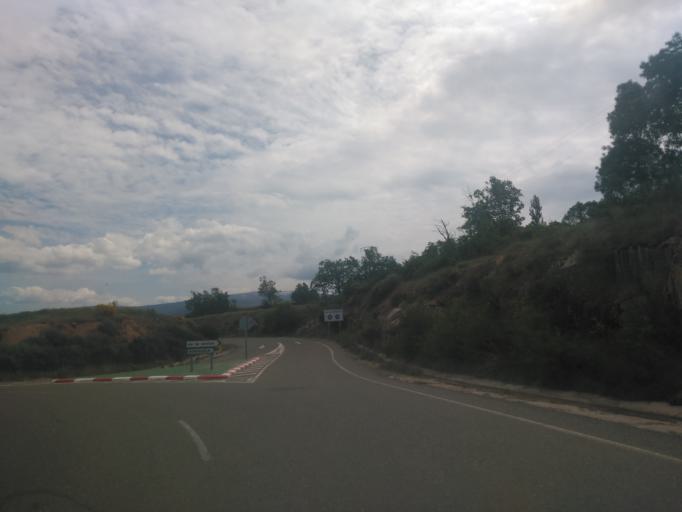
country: ES
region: Castille and Leon
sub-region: Provincia de Salamanca
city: Nava de Bejar
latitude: 40.4638
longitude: -5.6788
